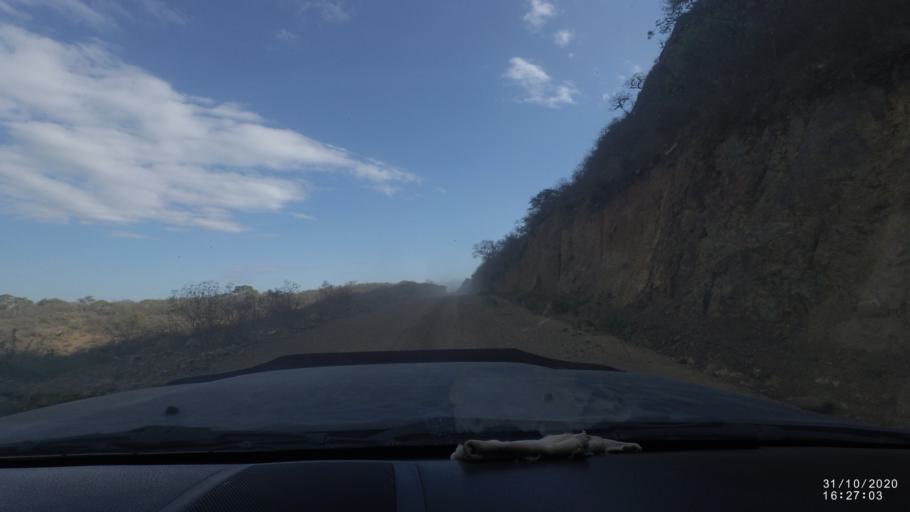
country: BO
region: Chuquisaca
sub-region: Provincia Zudanez
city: Mojocoya
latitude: -18.4034
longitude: -64.5857
